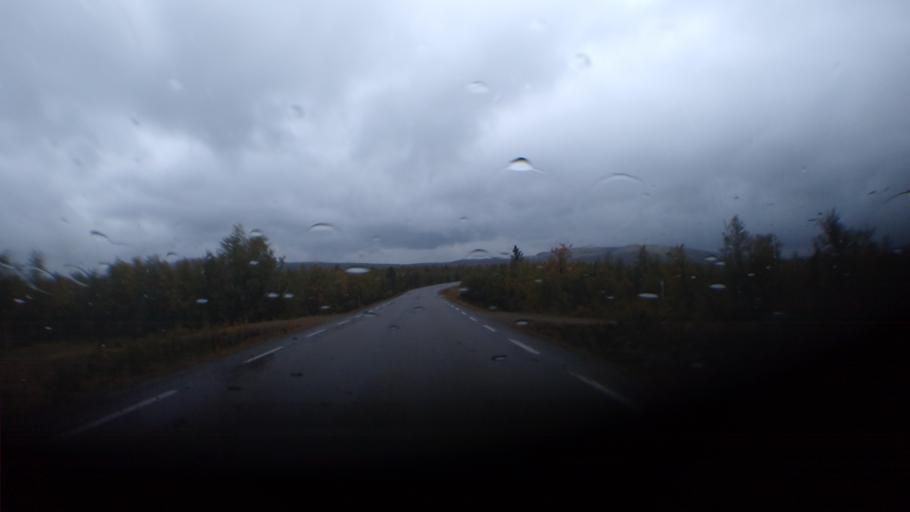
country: NO
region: Oppland
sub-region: Ringebu
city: Ringebu
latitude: 61.6571
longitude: 10.1185
